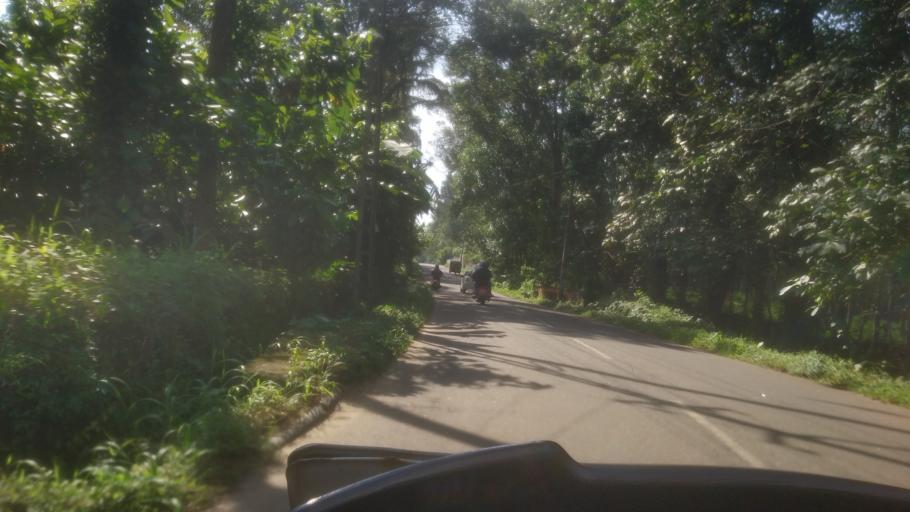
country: IN
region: Kerala
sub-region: Ernakulam
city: Kotamangalam
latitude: 10.0039
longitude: 76.6994
